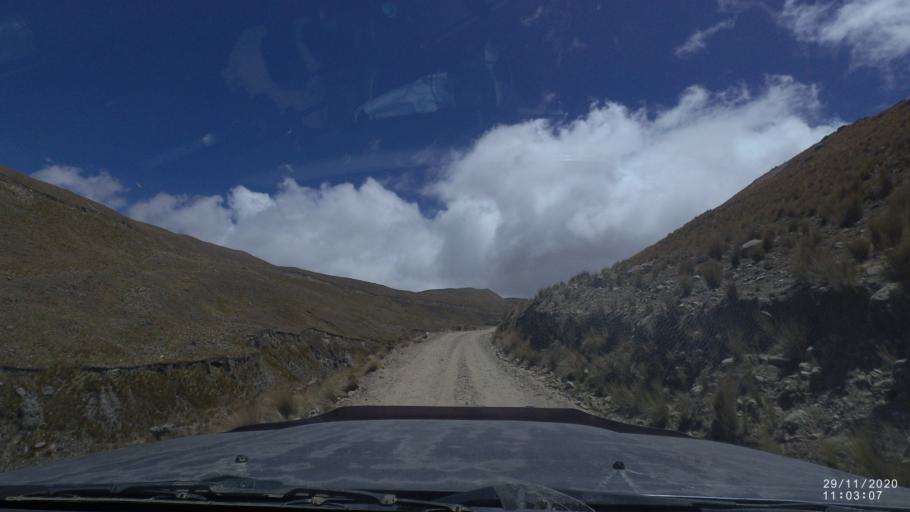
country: BO
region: Cochabamba
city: Cochabamba
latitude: -17.1913
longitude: -66.2227
